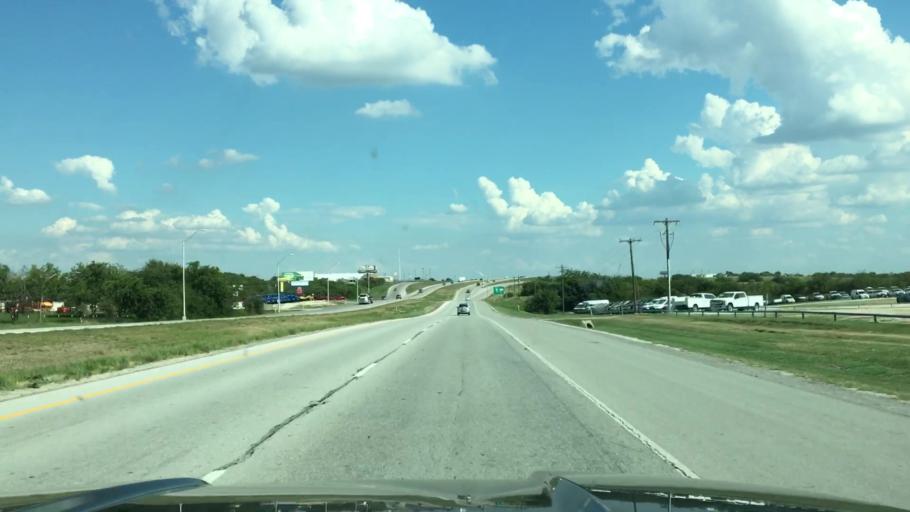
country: US
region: Texas
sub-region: Wise County
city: Decatur
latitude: 33.2104
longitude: -97.5764
